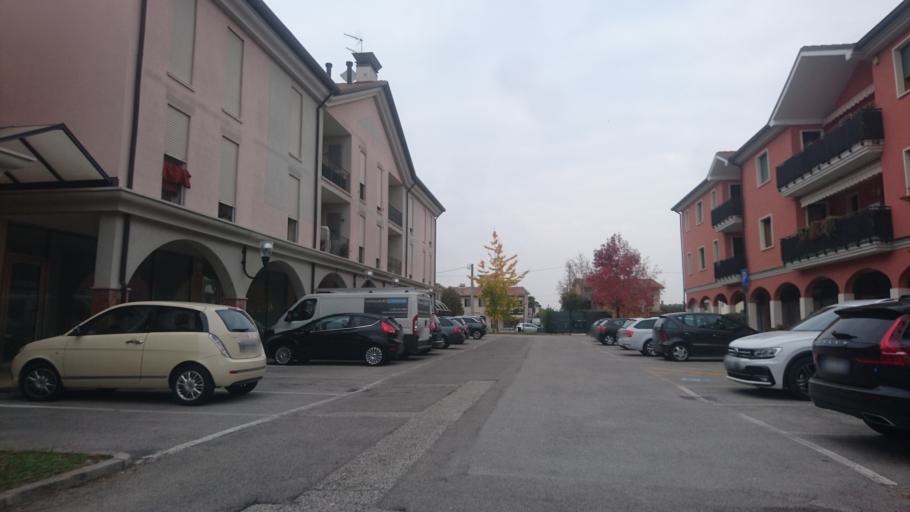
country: IT
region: Veneto
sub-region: Provincia di Venezia
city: Tombelle
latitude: 45.3954
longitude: 11.9828
